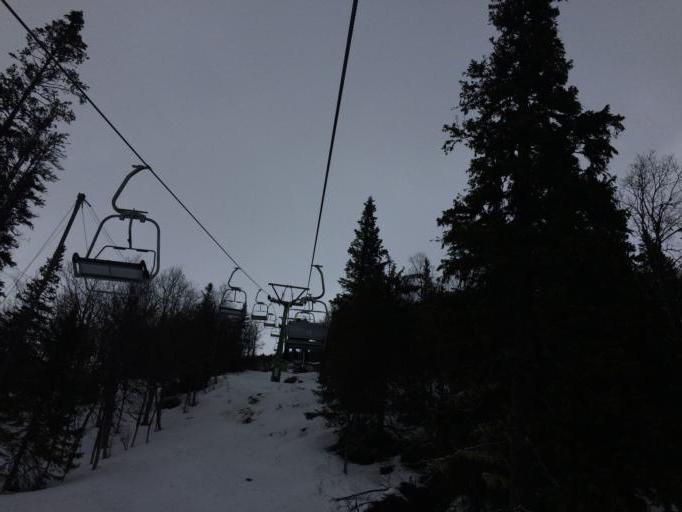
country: SE
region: Jaemtland
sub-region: Are Kommun
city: Are
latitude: 63.4079
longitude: 13.0788
